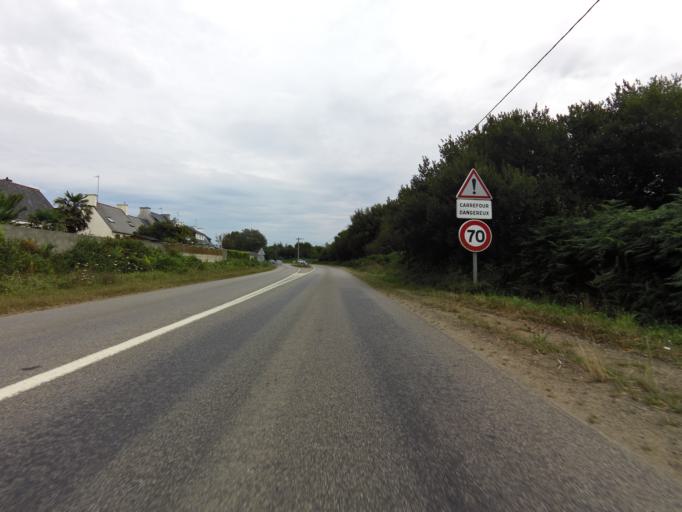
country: FR
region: Brittany
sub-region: Departement du Finistere
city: Poullan-sur-Mer
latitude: 48.0834
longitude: -4.3737
